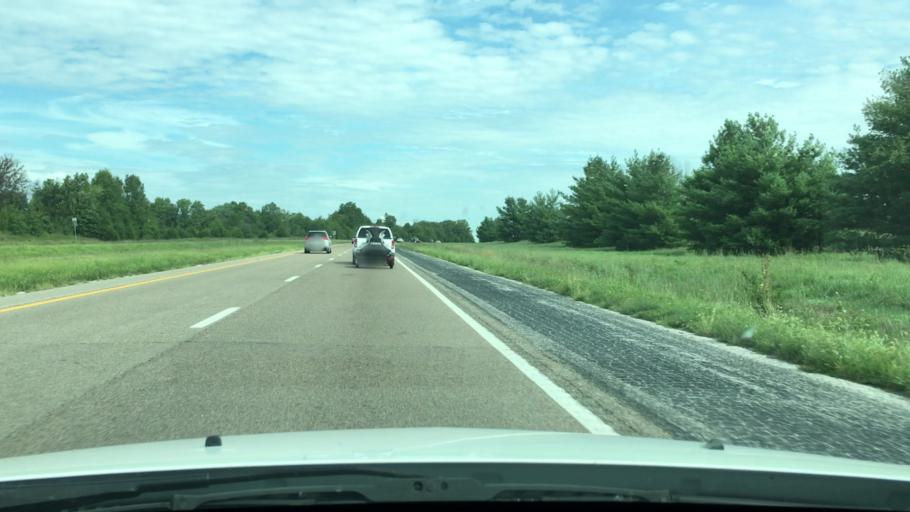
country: US
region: Missouri
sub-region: Audrain County
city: Mexico
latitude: 39.0052
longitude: -91.8930
